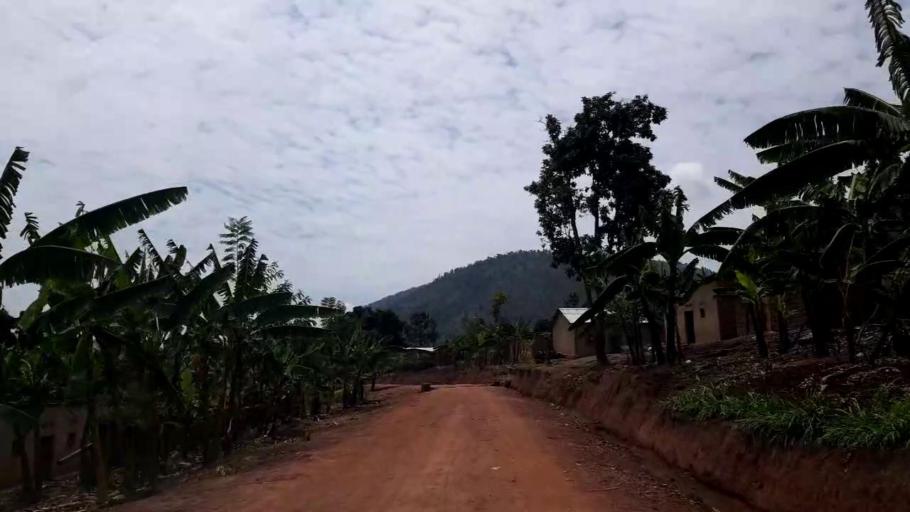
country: RW
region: Northern Province
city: Byumba
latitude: -1.5043
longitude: 30.1935
